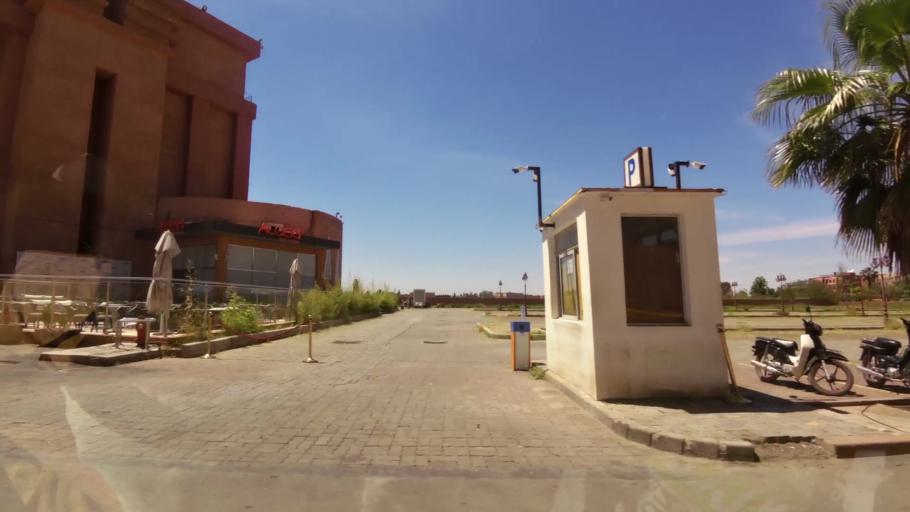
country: MA
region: Marrakech-Tensift-Al Haouz
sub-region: Marrakech
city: Marrakesh
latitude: 31.6251
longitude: -8.0170
